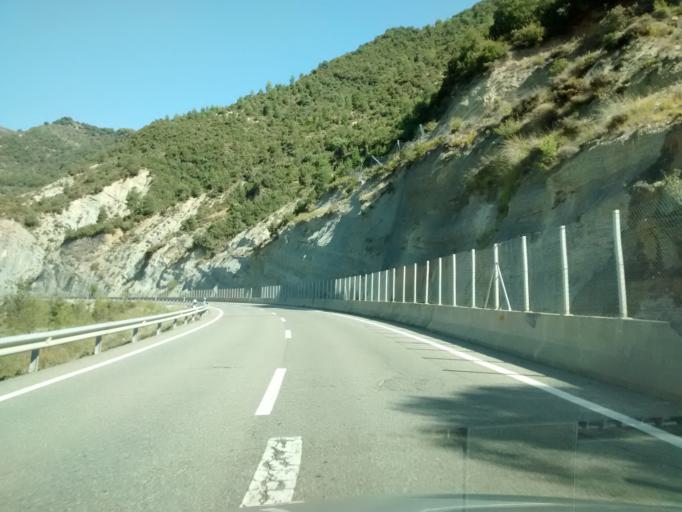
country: ES
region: Aragon
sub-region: Provincia de Huesca
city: Boltana
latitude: 42.4626
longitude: 0.0524
